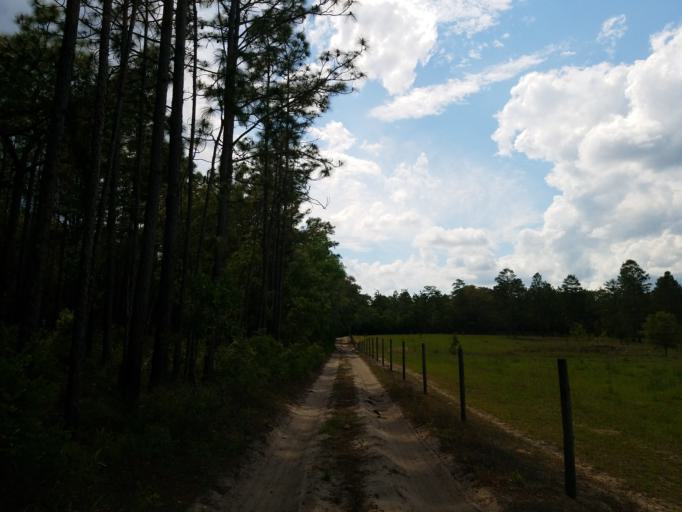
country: US
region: Florida
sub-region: Hernando County
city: Hill 'n Dale
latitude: 28.5502
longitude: -82.2706
